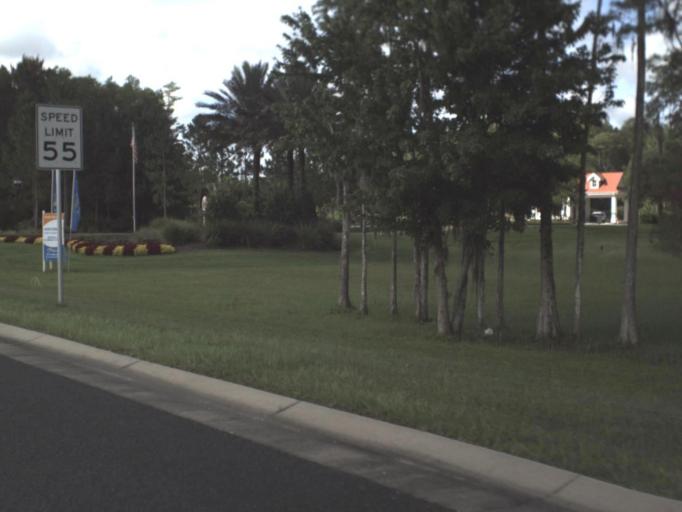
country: US
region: Florida
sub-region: Pasco County
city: Land O' Lakes
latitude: 28.2859
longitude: -82.4872
